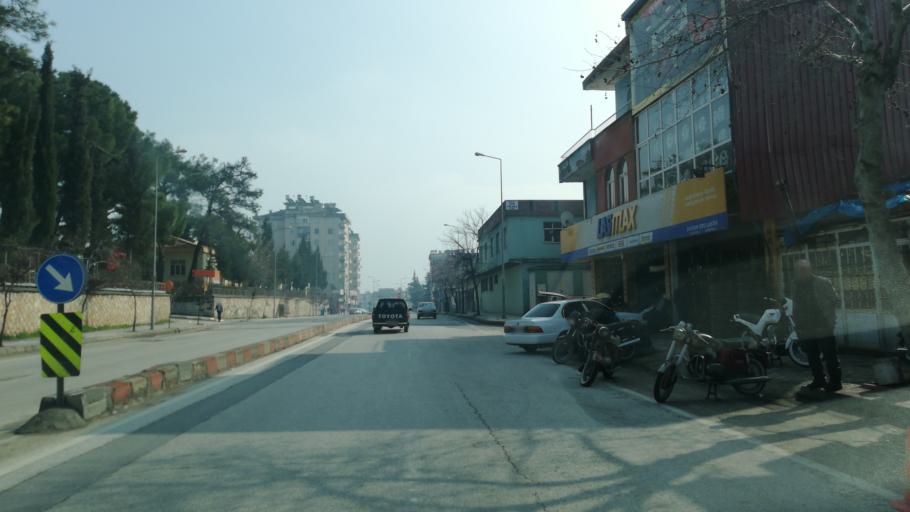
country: TR
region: Kahramanmaras
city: Kahramanmaras
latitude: 37.5734
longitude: 36.9391
